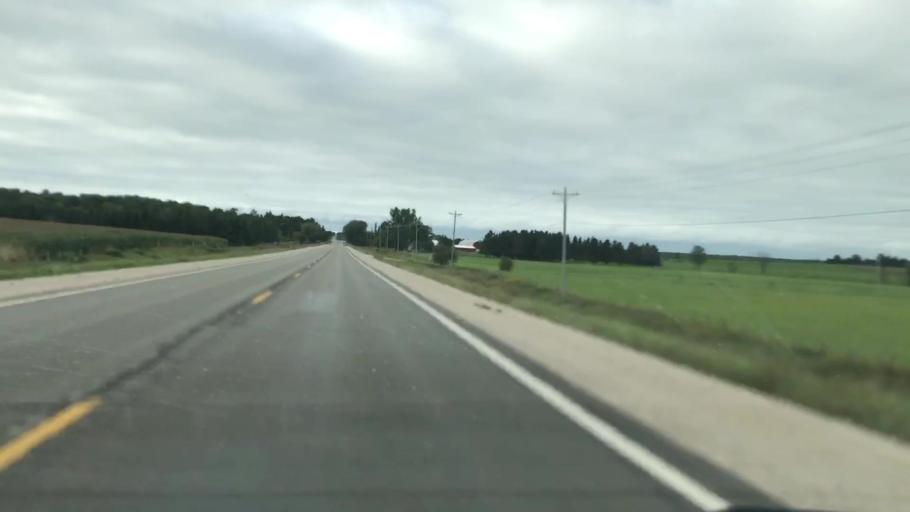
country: US
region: Michigan
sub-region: Luce County
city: Newberry
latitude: 46.1619
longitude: -85.5713
